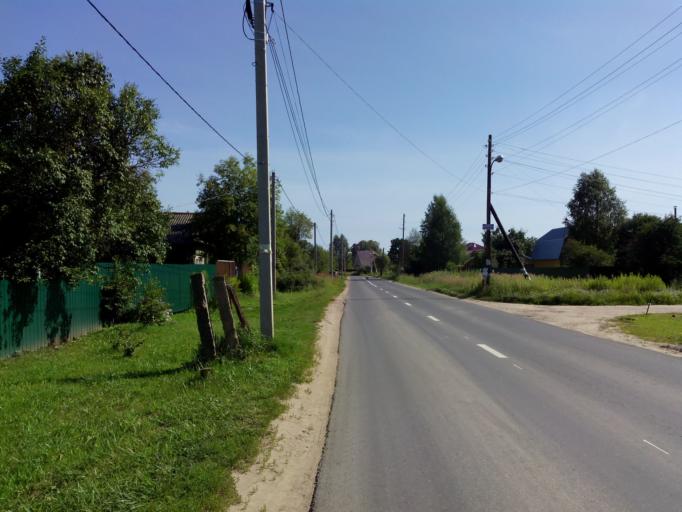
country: RU
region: Moskovskaya
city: Verbilki
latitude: 56.5426
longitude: 37.6130
